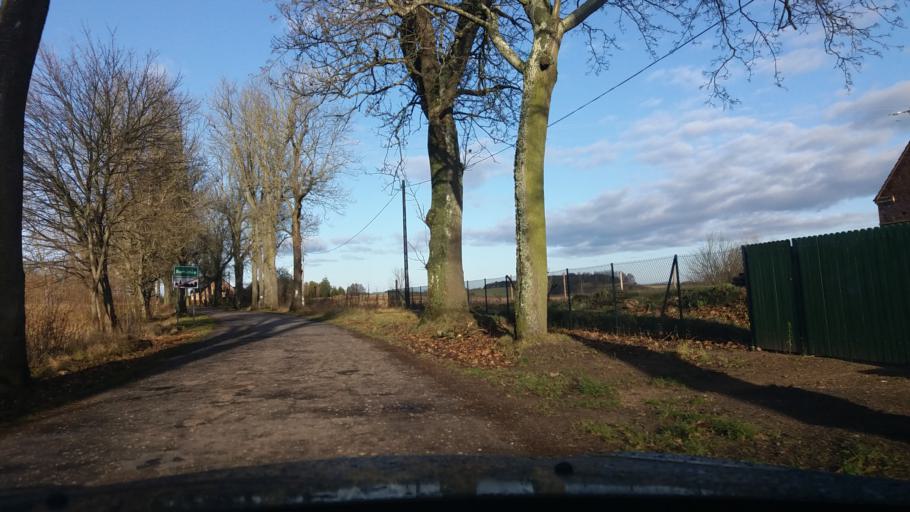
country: PL
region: West Pomeranian Voivodeship
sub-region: Powiat choszczenski
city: Drawno
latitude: 53.1799
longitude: 15.8040
